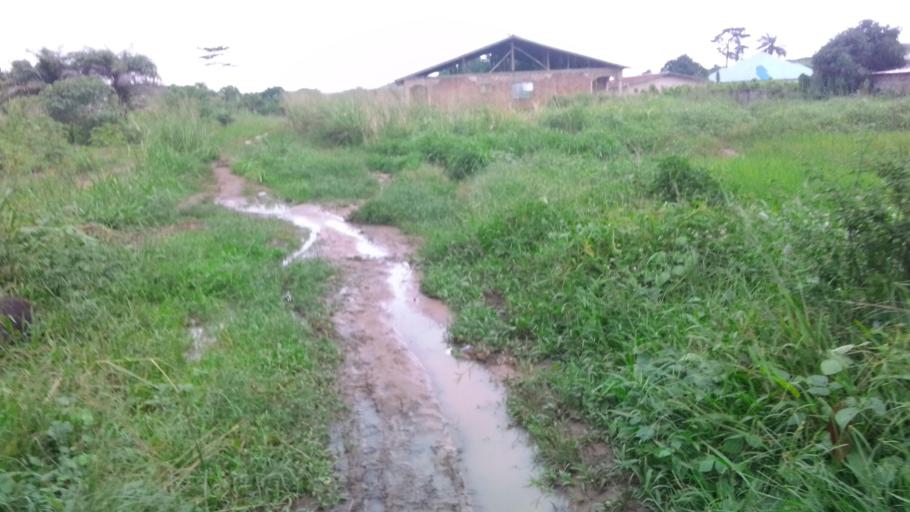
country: SL
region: Eastern Province
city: Kenema
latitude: 7.8445
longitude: -11.2003
